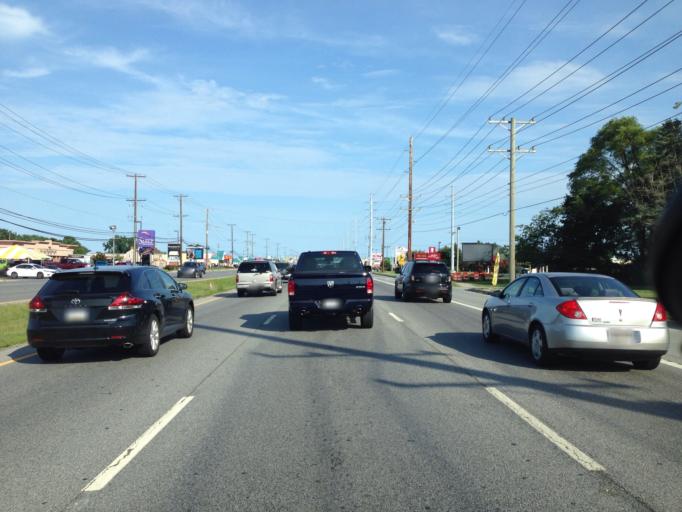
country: US
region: Delaware
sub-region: Sussex County
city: Lewes
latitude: 38.7398
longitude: -75.1460
